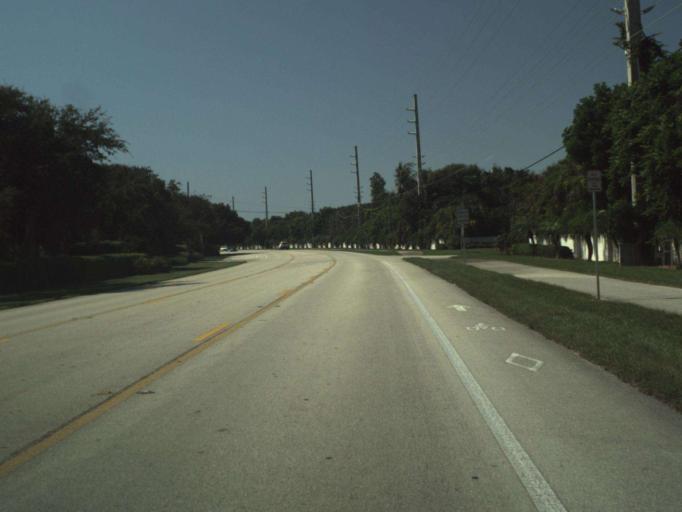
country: US
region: Florida
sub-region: Indian River County
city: Indian River Shores
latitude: 27.6781
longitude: -80.3656
